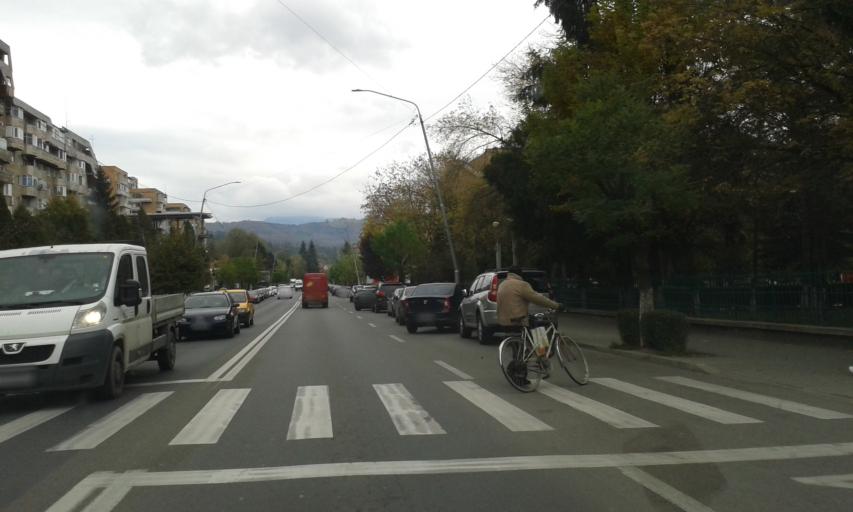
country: RO
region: Hunedoara
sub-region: Municipiul Petrosani
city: Petrosani
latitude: 45.4141
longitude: 23.3744
